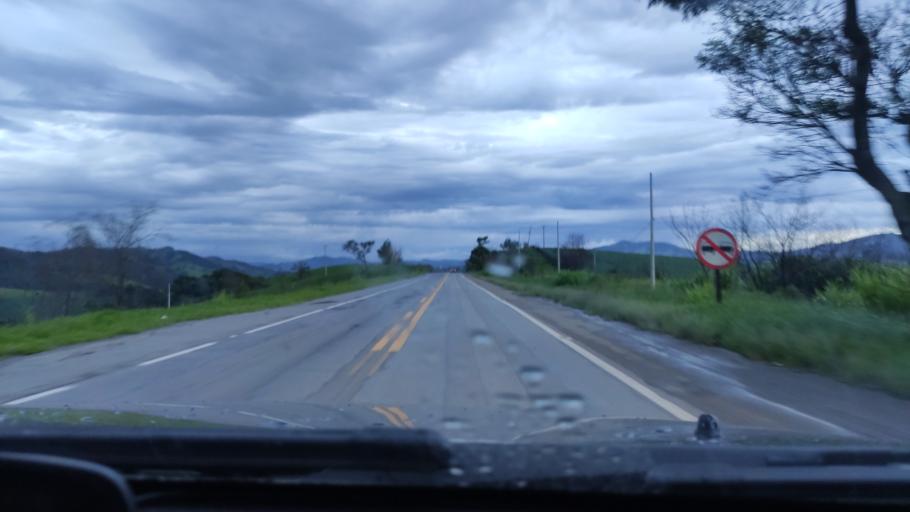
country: BR
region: Sao Paulo
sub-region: Socorro
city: Socorro
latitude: -22.6690
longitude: -46.5570
